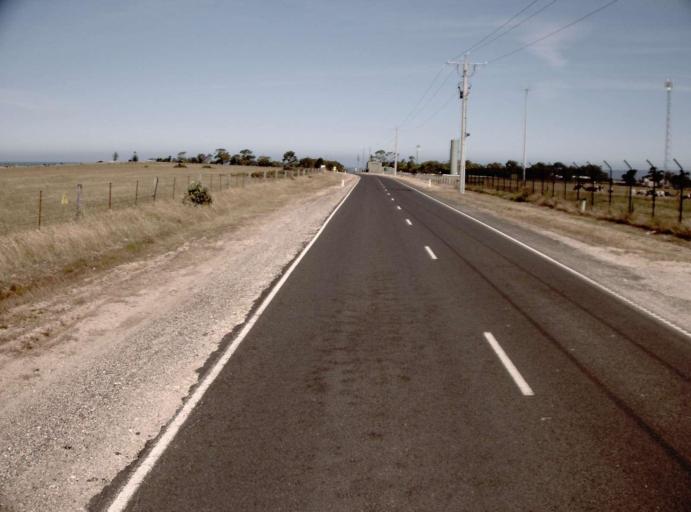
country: AU
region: Victoria
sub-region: Wellington
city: Sale
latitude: -38.3580
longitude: 147.1744
